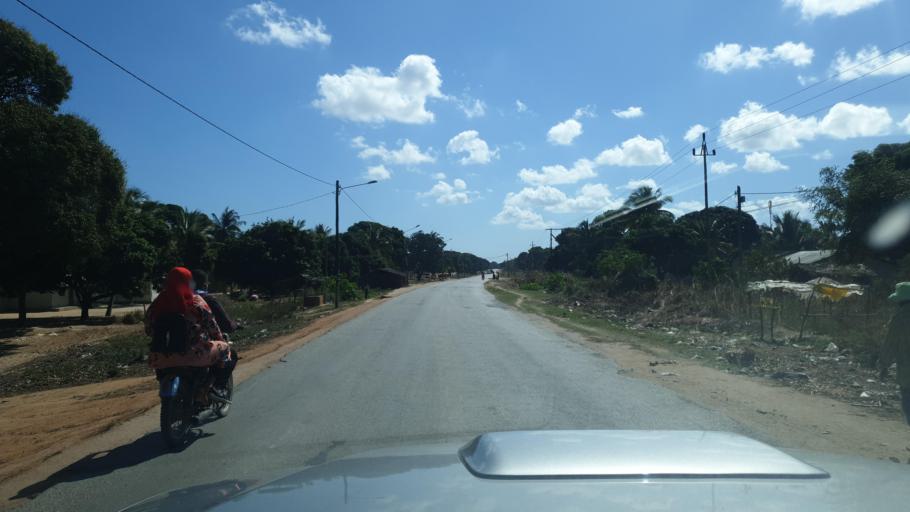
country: MZ
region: Nampula
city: Nacala
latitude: -14.5187
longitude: 40.6957
